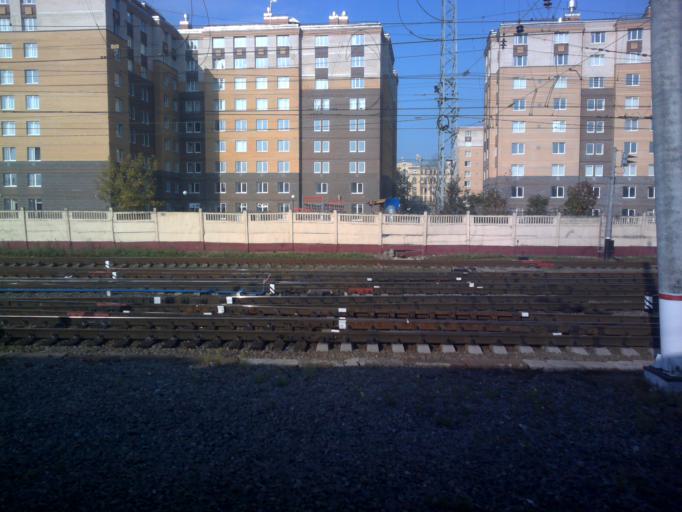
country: RU
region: Leningrad
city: Finlyandskiy
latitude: 59.9610
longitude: 30.3593
